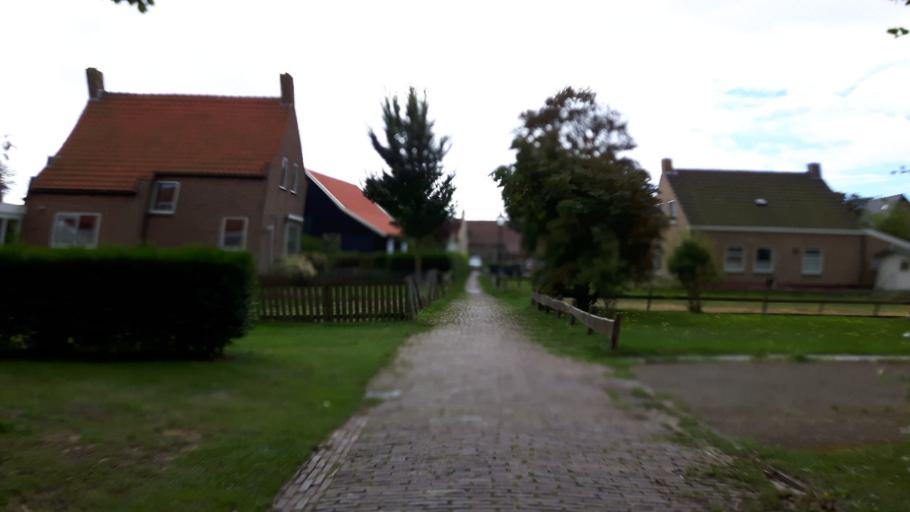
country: NL
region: Friesland
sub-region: Gemeente Ameland
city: Hollum
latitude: 53.4400
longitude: 5.6379
